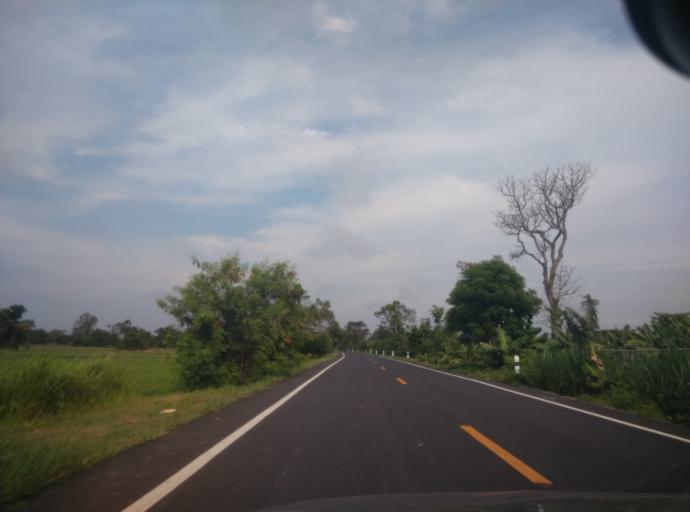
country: TH
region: Sisaket
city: Si Sa Ket
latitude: 15.1223
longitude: 104.2377
